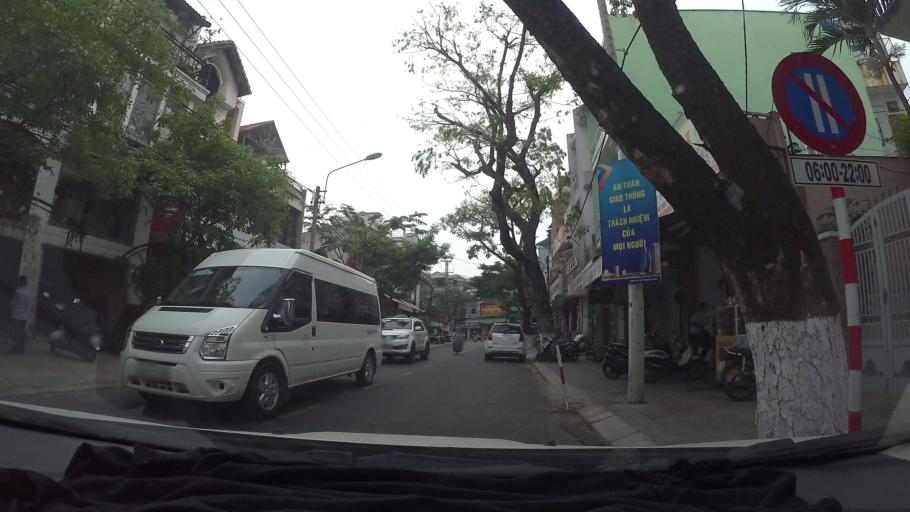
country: VN
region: Da Nang
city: Da Nang
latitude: 16.0642
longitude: 108.2193
